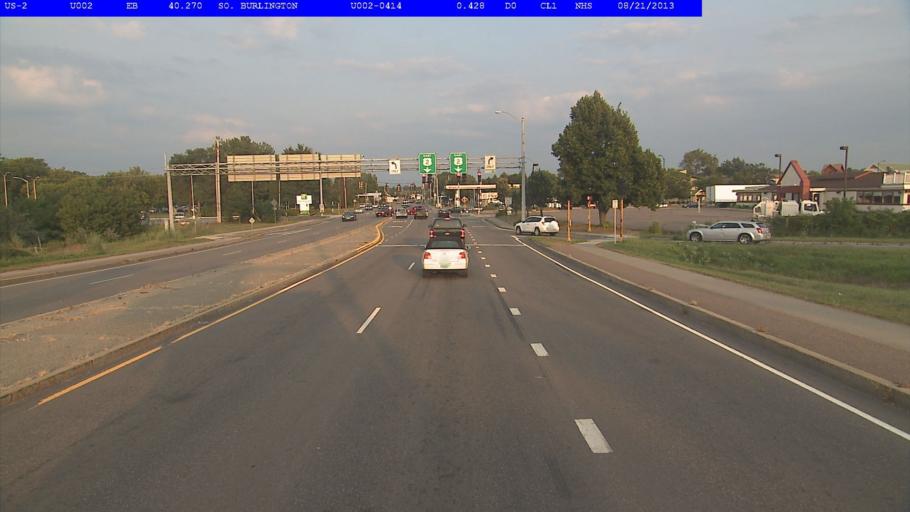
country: US
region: Vermont
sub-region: Chittenden County
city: South Burlington
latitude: 44.4695
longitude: -73.1827
